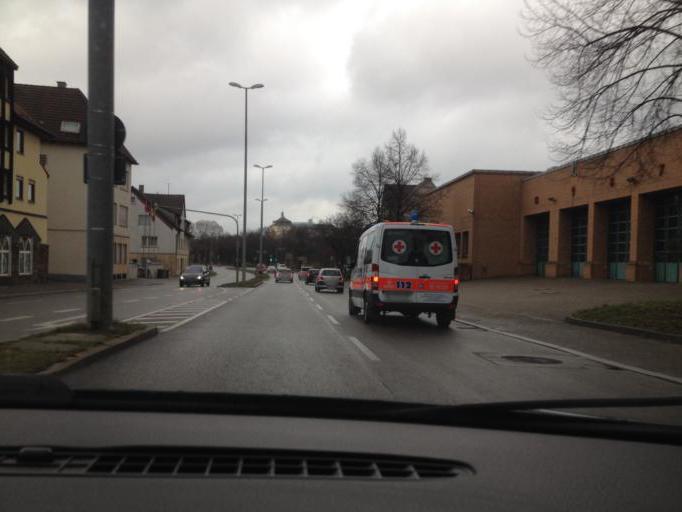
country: DE
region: Baden-Wuerttemberg
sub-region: Regierungsbezirk Stuttgart
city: Ludwigsburg
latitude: 48.9024
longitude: 9.1879
